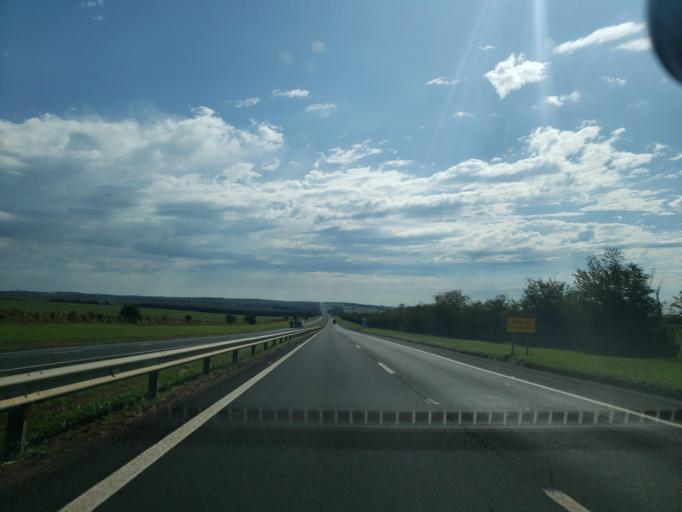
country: BR
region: Sao Paulo
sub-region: Pirajui
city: Pirajui
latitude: -21.9128
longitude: -49.5152
